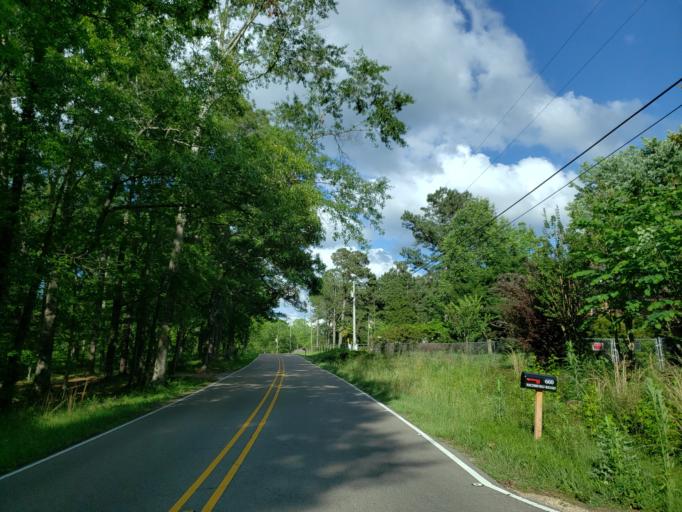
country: US
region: Mississippi
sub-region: Lamar County
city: West Hattiesburg
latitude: 31.2713
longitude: -89.3591
